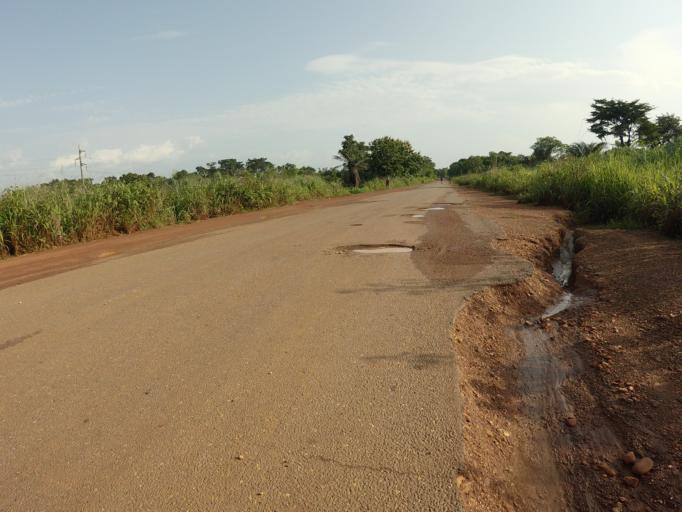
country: GH
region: Volta
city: Hohoe
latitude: 7.0608
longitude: 0.4308
